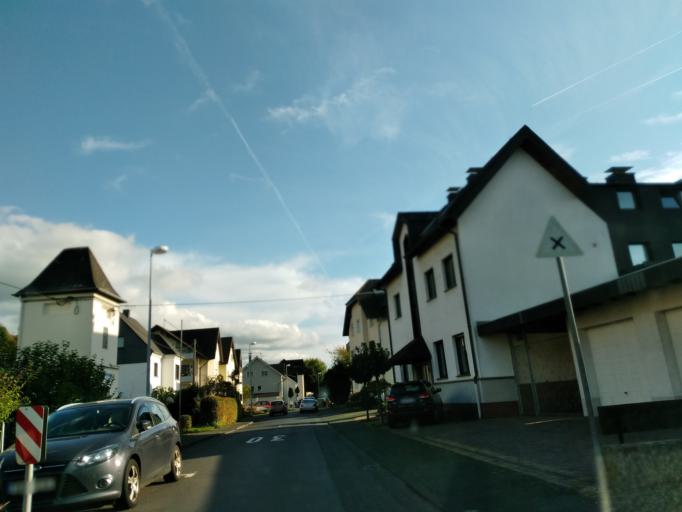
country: DE
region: Rheinland-Pfalz
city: Erpel
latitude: 50.5871
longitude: 7.2330
